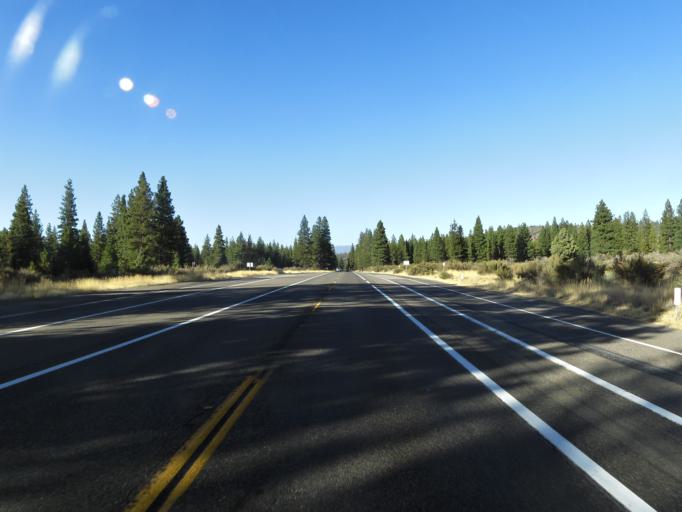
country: US
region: California
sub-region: Siskiyou County
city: Weed
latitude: 41.4528
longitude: -122.3607
